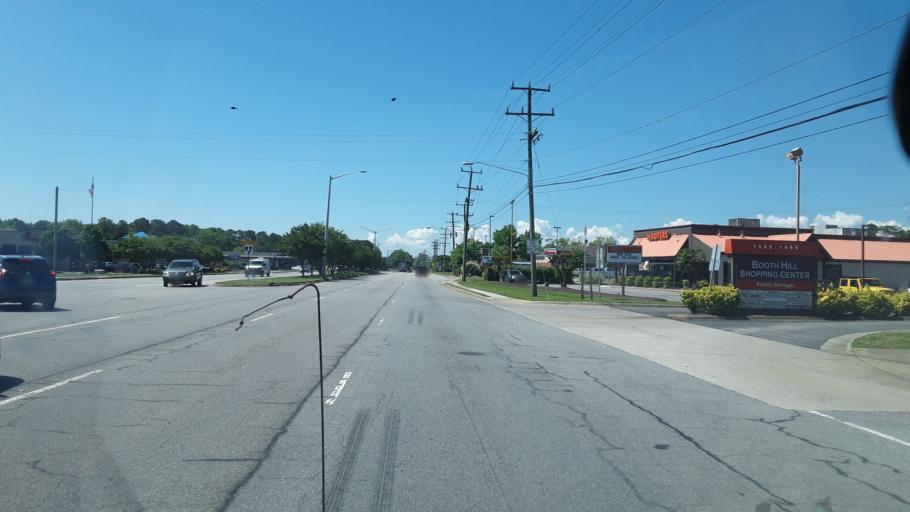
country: US
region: Virginia
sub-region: City of Virginia Beach
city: Virginia Beach
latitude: 36.7894
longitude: -75.9976
